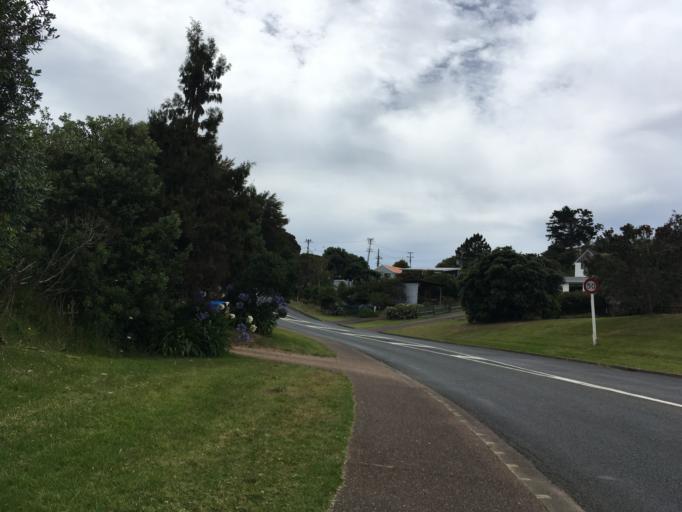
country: NZ
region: Auckland
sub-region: Auckland
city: Pakuranga
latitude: -36.7897
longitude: 175.0236
